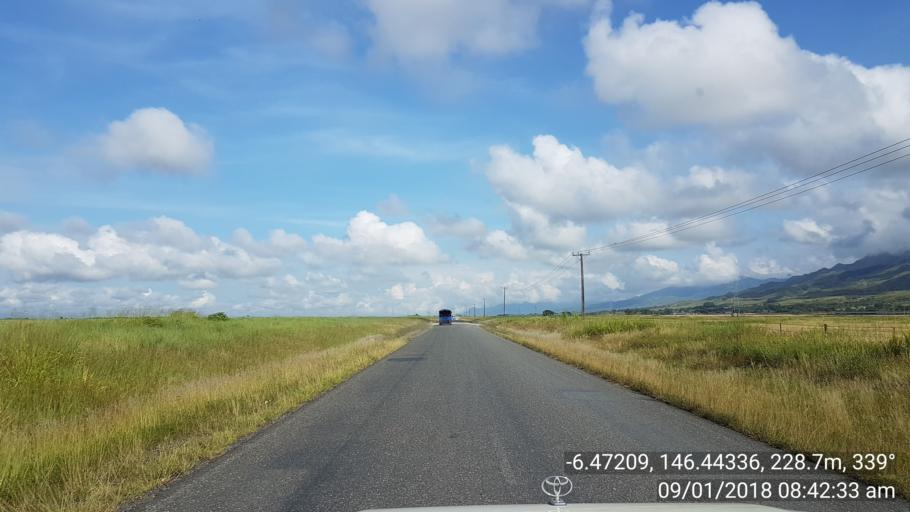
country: PG
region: Morobe
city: Lae
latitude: -6.4722
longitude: 146.4436
